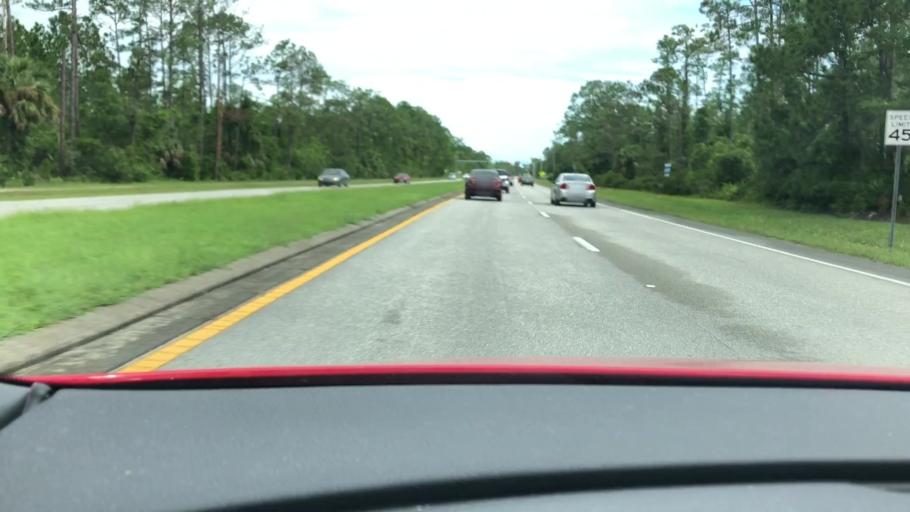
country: US
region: Florida
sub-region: Volusia County
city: Holly Hill
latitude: 29.2338
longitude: -81.0894
